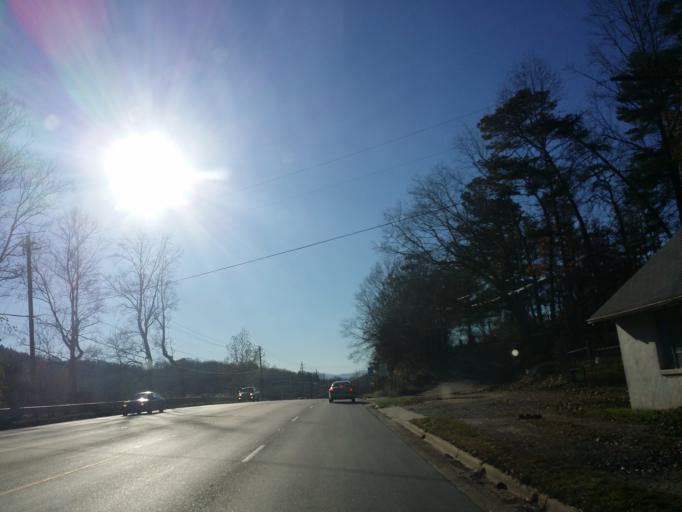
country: US
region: North Carolina
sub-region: Buncombe County
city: Swannanoa
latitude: 35.5852
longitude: -82.4599
